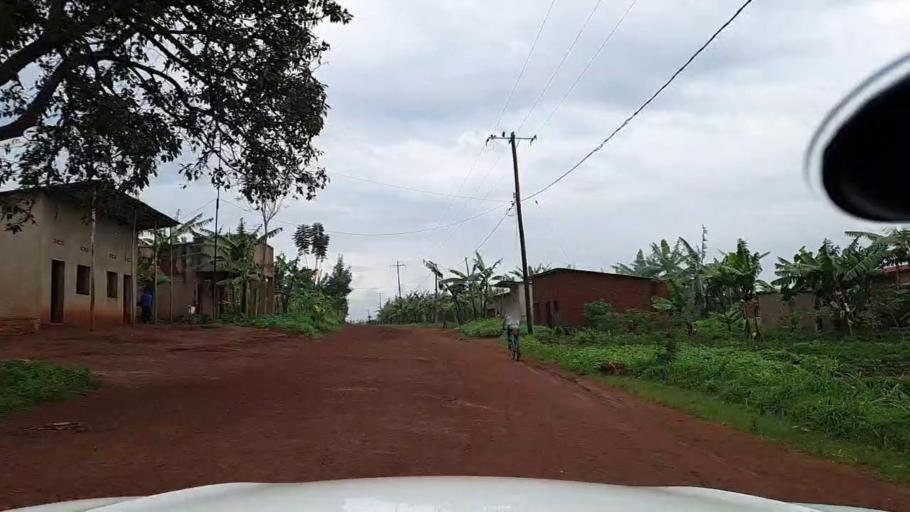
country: RW
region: Kigali
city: Kigali
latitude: -1.9167
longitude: 29.8985
